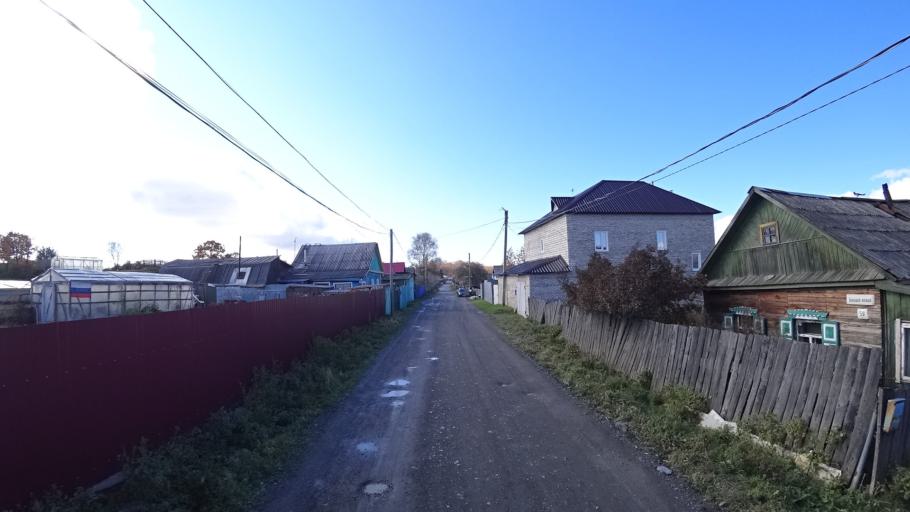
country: RU
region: Khabarovsk Krai
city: Amursk
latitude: 50.2338
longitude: 136.9191
